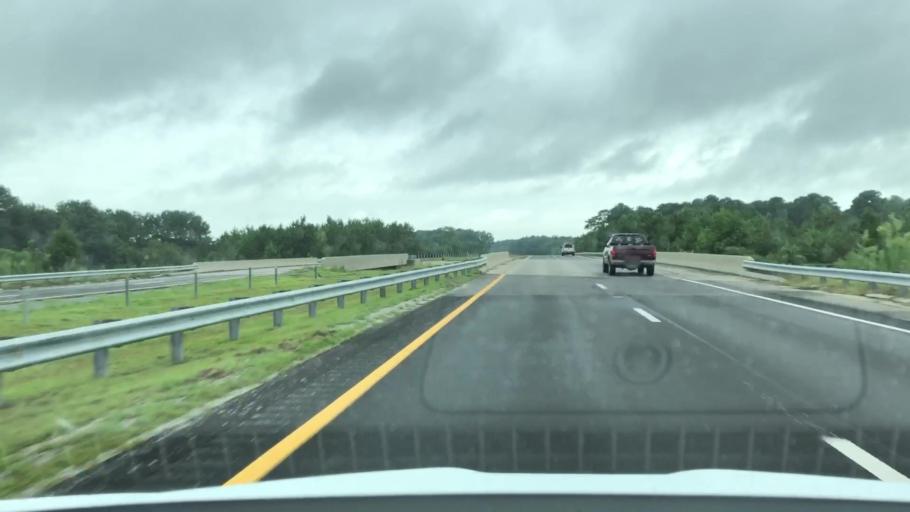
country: US
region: North Carolina
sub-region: Wayne County
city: Fremont
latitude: 35.4686
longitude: -77.9865
